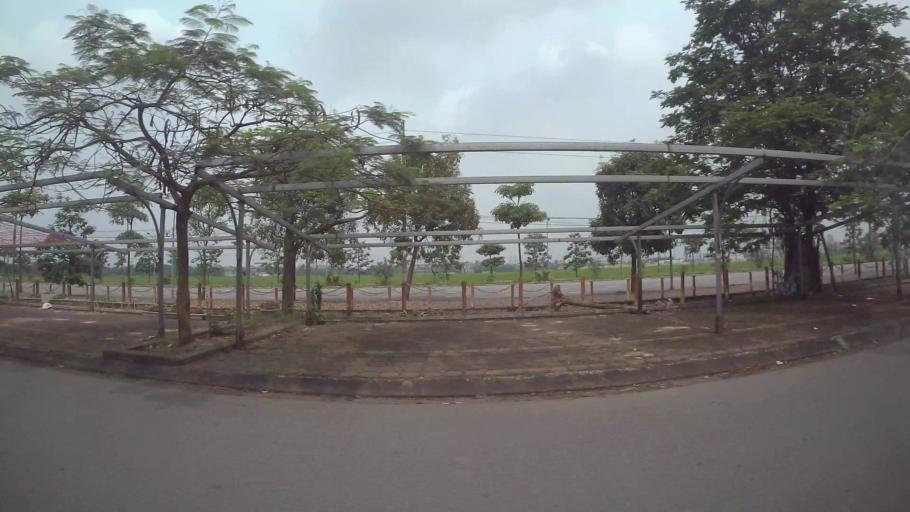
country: VN
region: Ha Noi
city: Trau Quy
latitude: 21.0681
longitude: 105.9108
